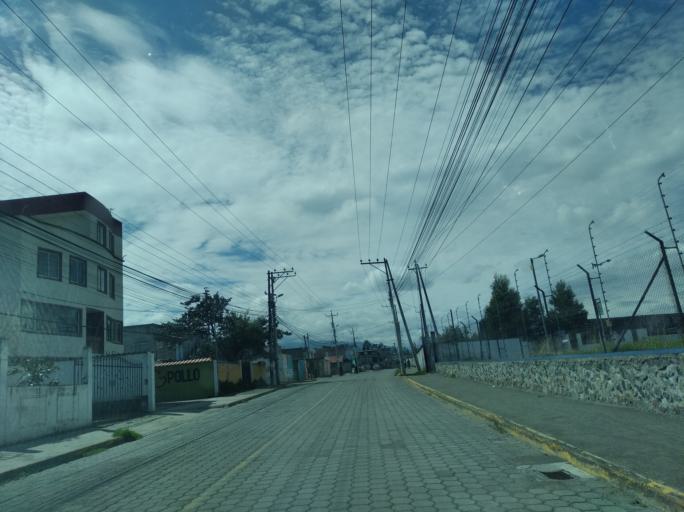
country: EC
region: Pichincha
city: Sangolqui
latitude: -0.2147
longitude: -78.3398
